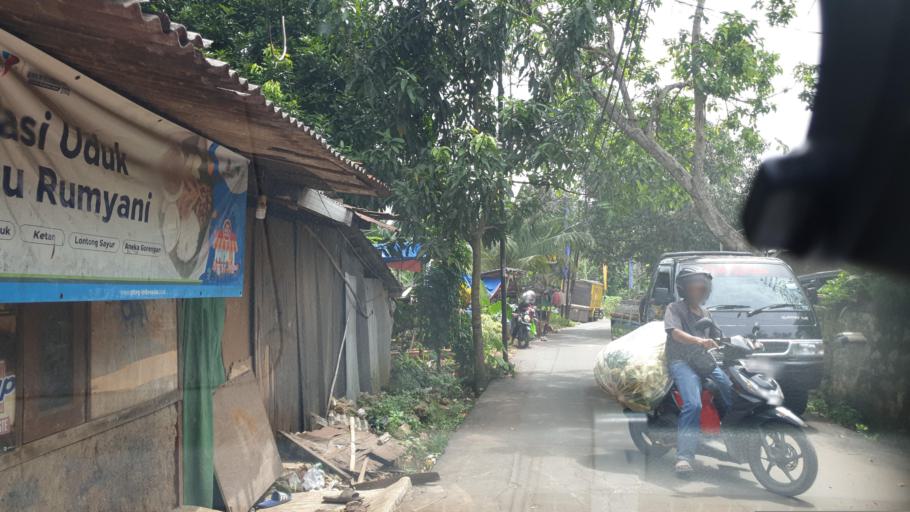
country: ID
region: West Java
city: Sawangan
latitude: -6.3768
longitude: 106.7625
